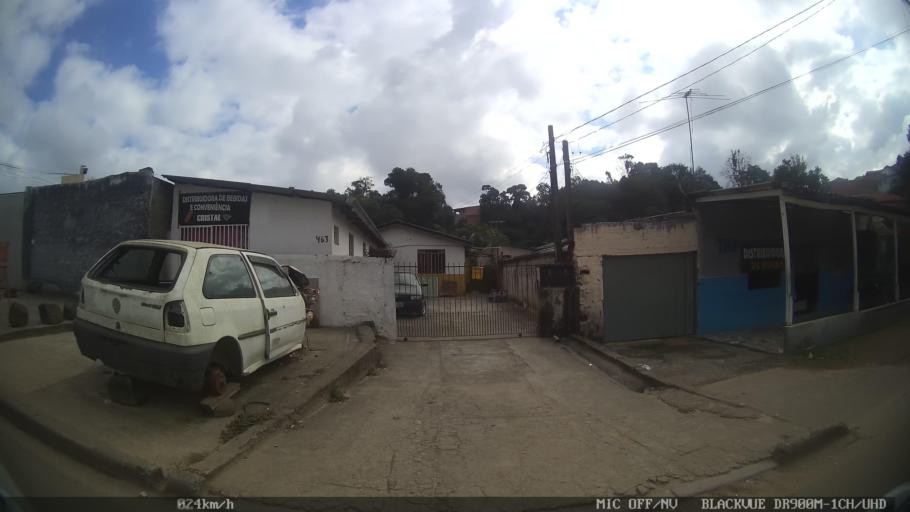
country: BR
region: Parana
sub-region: Almirante Tamandare
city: Almirante Tamandare
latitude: -25.3486
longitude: -49.2541
